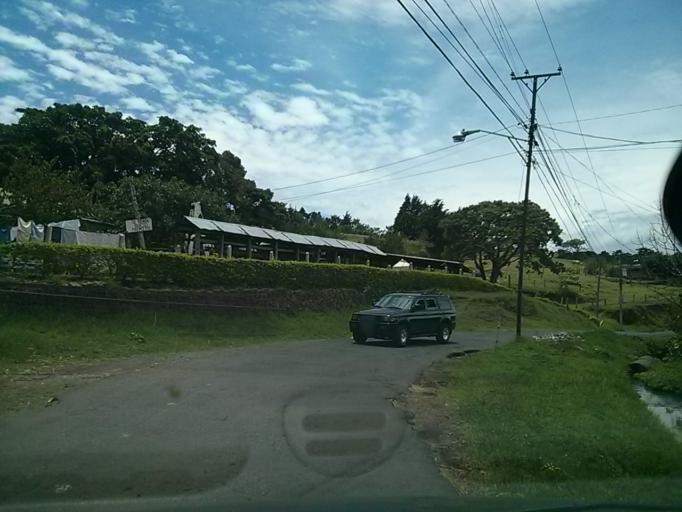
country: CR
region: Heredia
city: Santo Domingo
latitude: 10.0714
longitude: -84.1065
